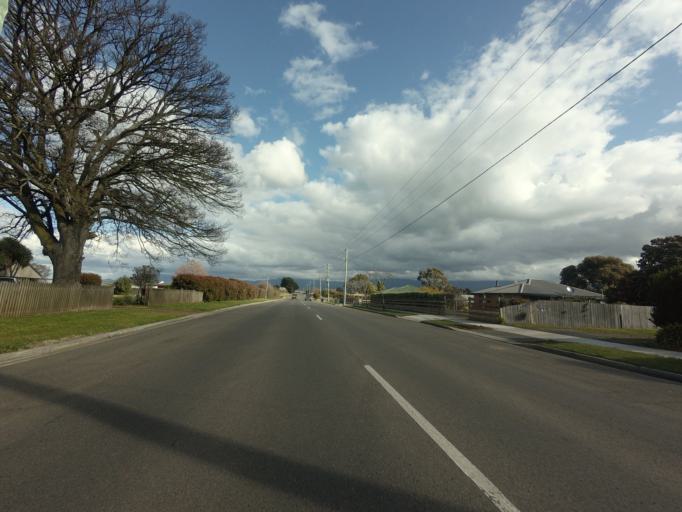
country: AU
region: Tasmania
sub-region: Northern Midlands
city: Longford
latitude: -41.6929
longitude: 147.0788
